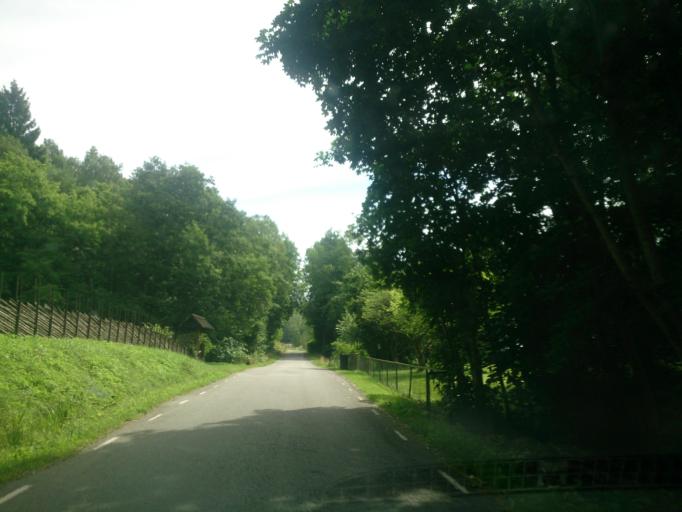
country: SE
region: OEstergoetland
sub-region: Atvidabergs Kommun
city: Atvidaberg
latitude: 58.3101
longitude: 16.0691
